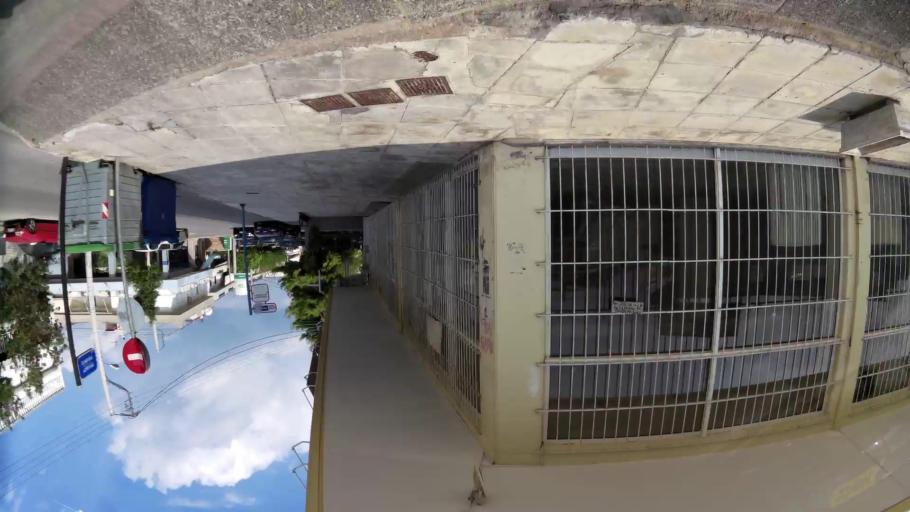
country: GR
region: Attica
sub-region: Nomarchia Athinas
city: Ilion
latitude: 38.0423
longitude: 23.7065
